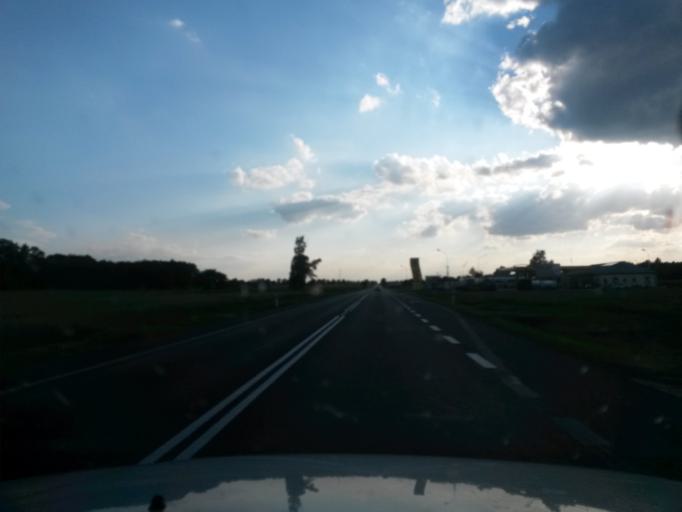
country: PL
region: Lodz Voivodeship
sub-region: Powiat belchatowski
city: Rusiec
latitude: 51.3160
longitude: 18.9452
